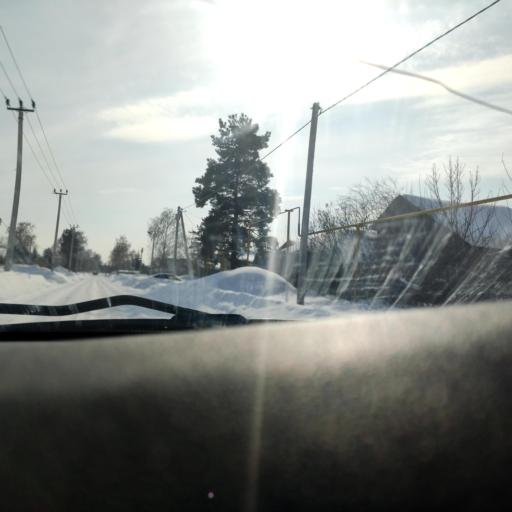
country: RU
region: Samara
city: Rozhdestveno
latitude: 53.2413
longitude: 50.0613
